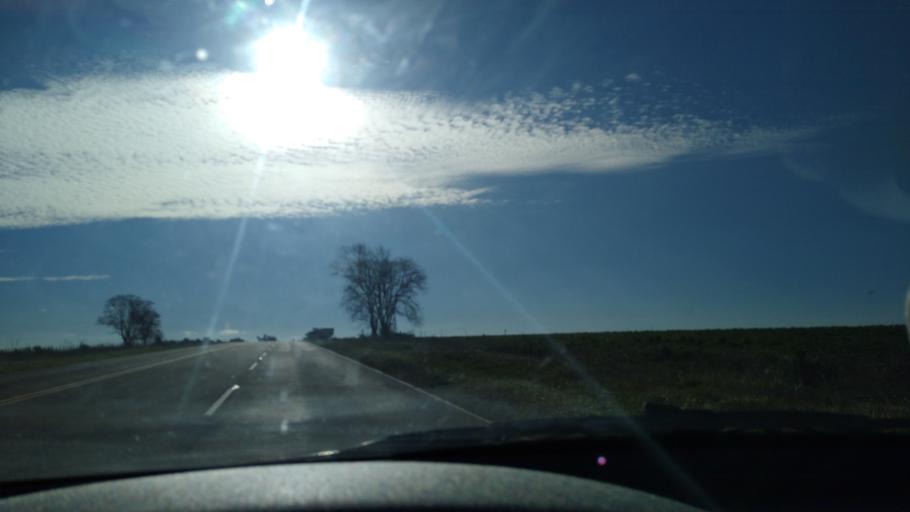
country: AR
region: Entre Rios
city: Aranguren
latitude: -32.3365
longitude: -60.3802
